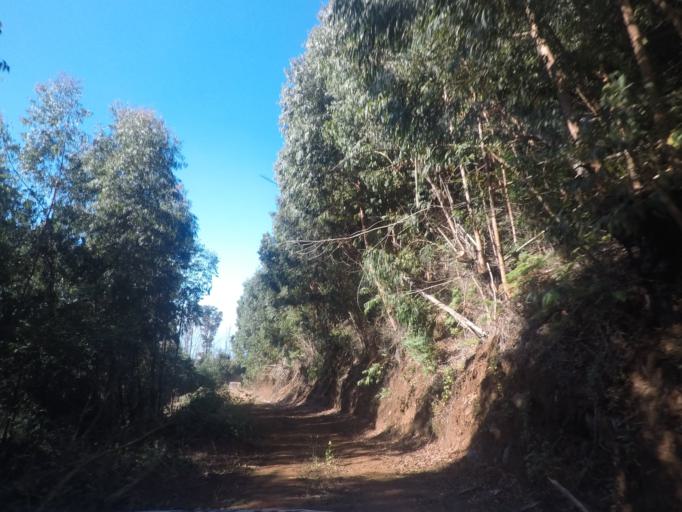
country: PT
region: Madeira
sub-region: Funchal
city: Nossa Senhora do Monte
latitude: 32.6923
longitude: -16.9122
